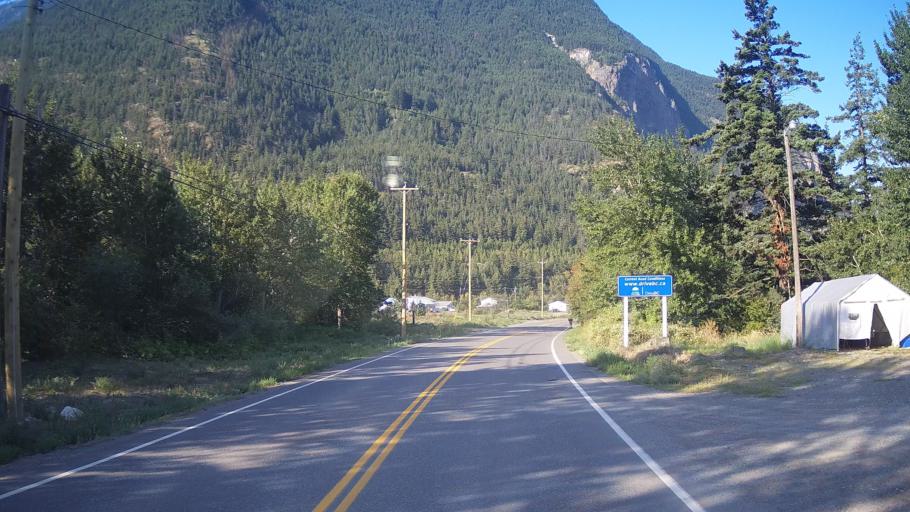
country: CA
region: British Columbia
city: Lillooet
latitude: 50.6745
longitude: -121.9362
